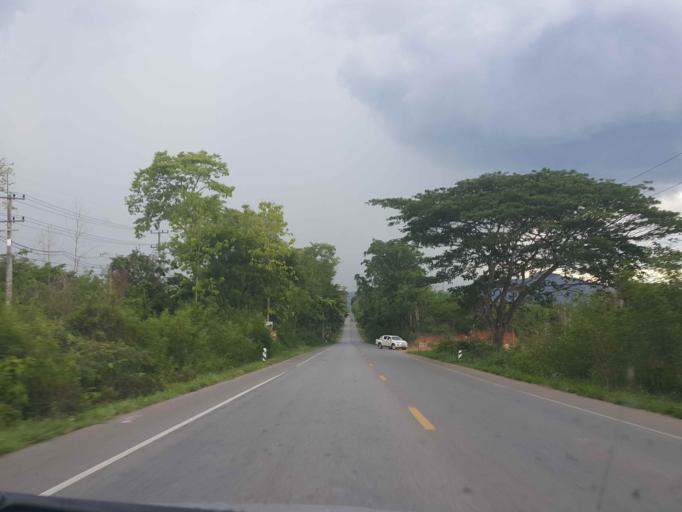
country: TH
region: Phrae
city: Den Chai
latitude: 17.9675
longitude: 100.0502
